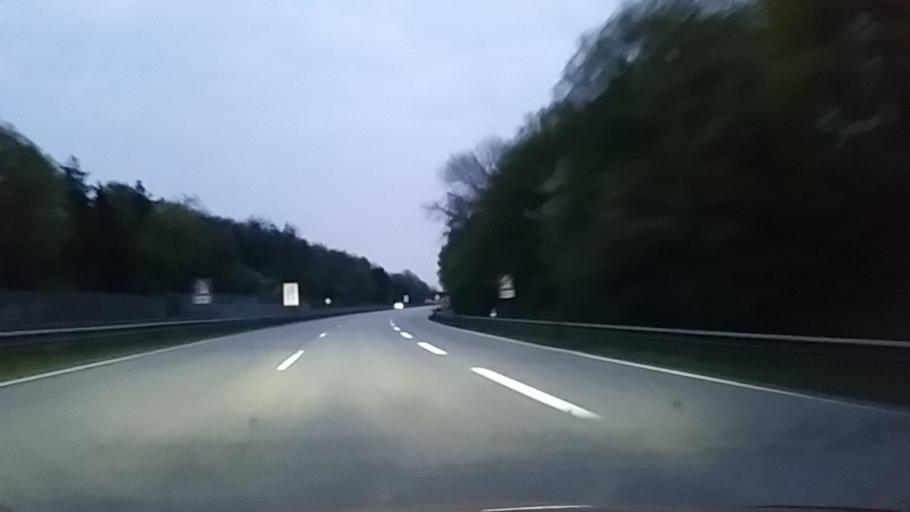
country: DE
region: Schleswig-Holstein
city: Ratekau
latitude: 53.9100
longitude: 10.7727
